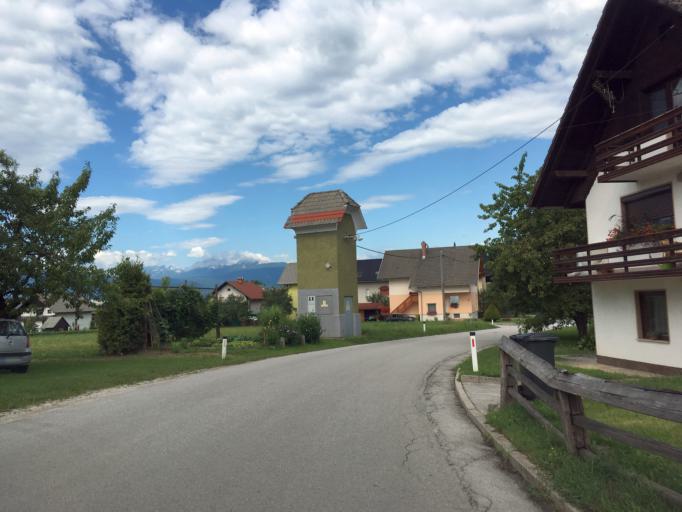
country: SI
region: Radovljica
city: Radovljica
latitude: 46.3746
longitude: 14.1945
